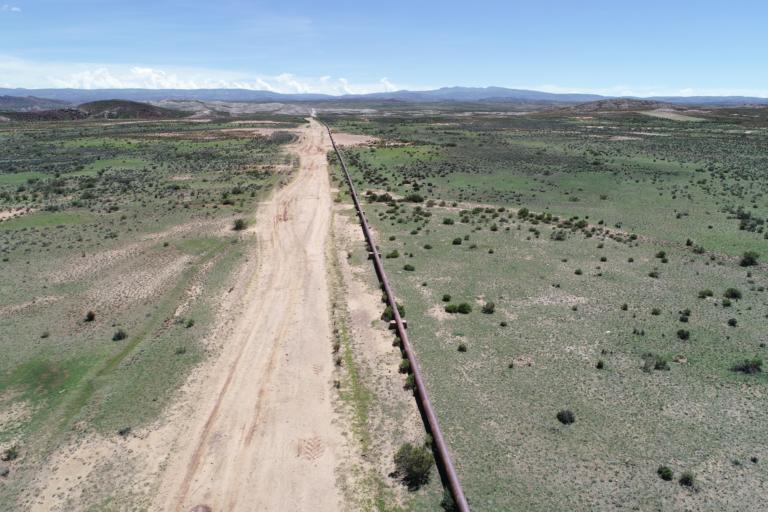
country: BO
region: La Paz
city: Patacamaya
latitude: -17.2757
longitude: -68.5080
